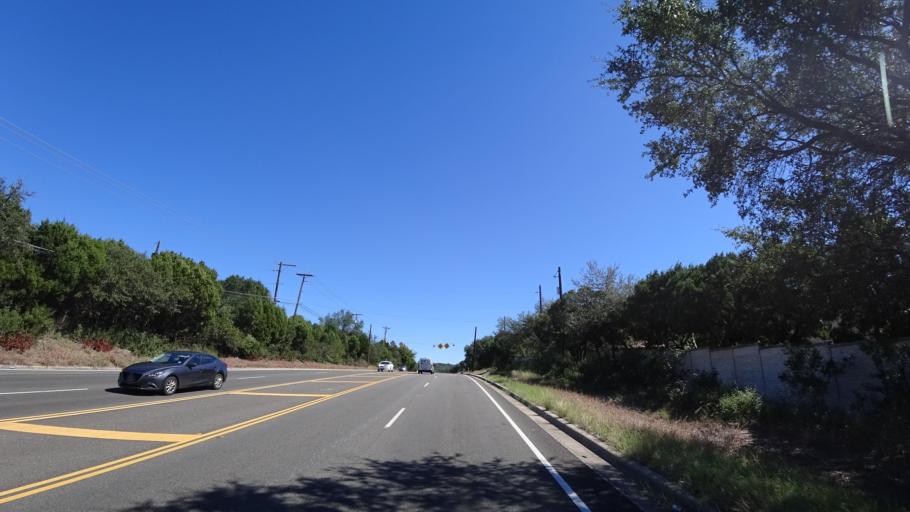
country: US
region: Texas
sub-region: Travis County
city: West Lake Hills
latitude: 30.3411
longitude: -97.7760
